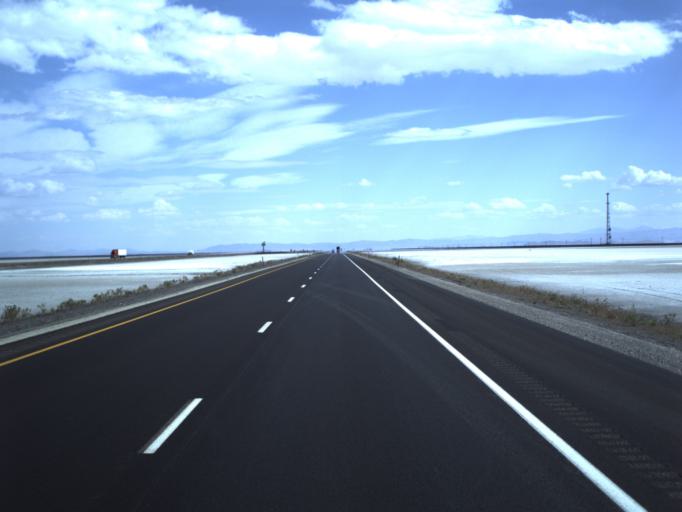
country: US
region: Utah
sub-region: Tooele County
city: Wendover
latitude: 40.7326
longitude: -113.5761
